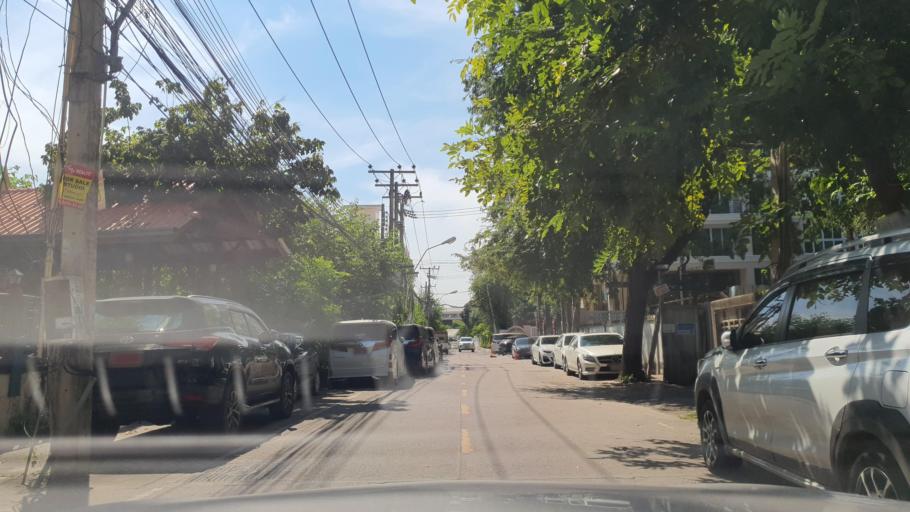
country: TH
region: Chon Buri
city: Phatthaya
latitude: 12.9535
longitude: 100.8837
